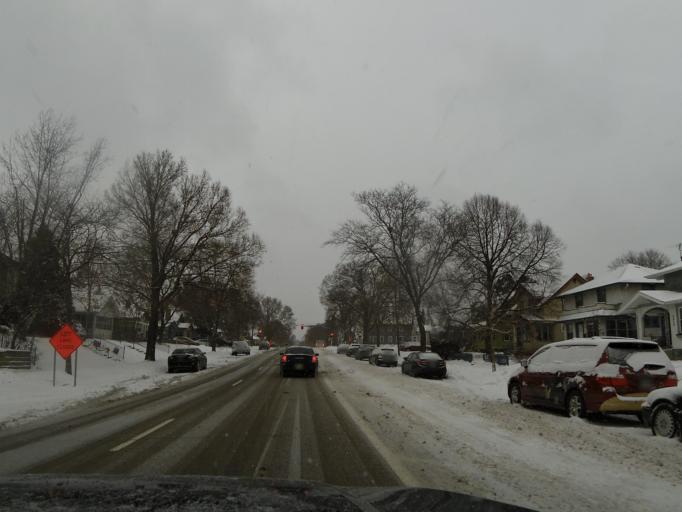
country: US
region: Minnesota
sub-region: Hennepin County
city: Minneapolis
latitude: 44.9330
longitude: -93.2649
